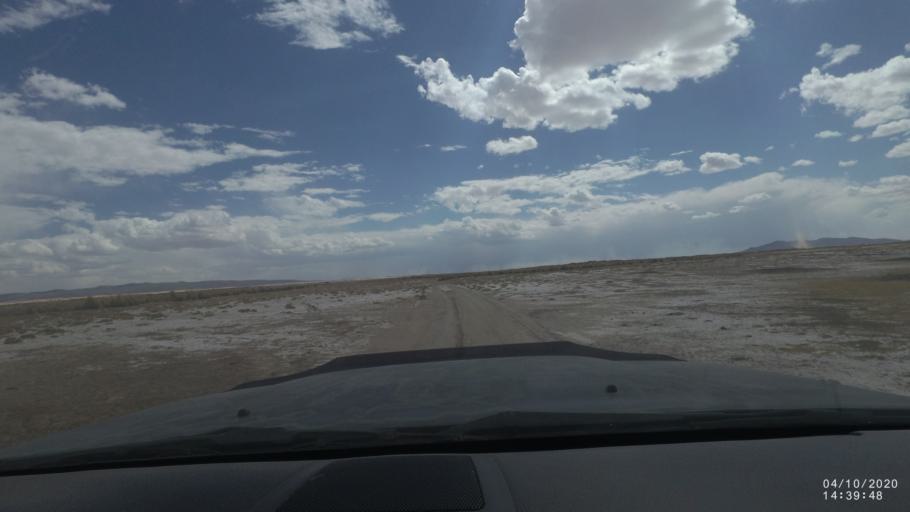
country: BO
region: Oruro
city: Poopo
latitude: -18.6780
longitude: -67.4880
